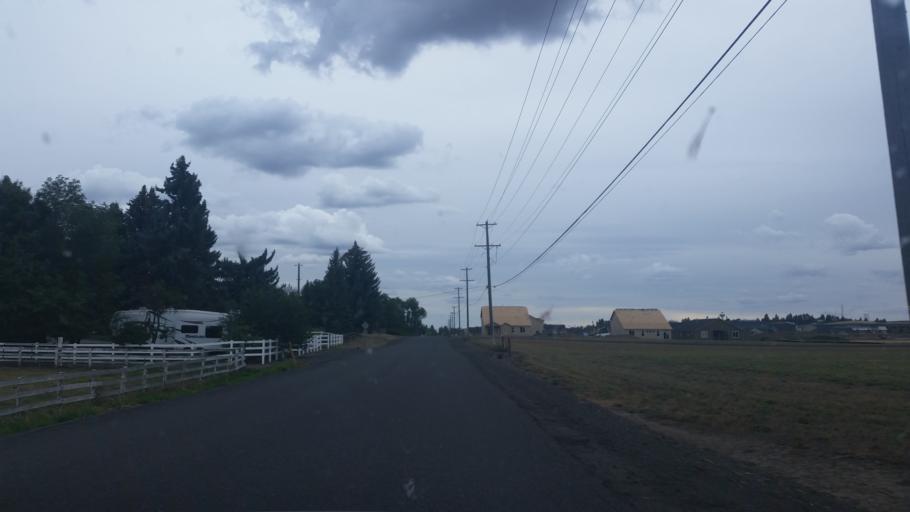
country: US
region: Washington
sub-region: Spokane County
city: Cheney
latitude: 47.5127
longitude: -117.5756
